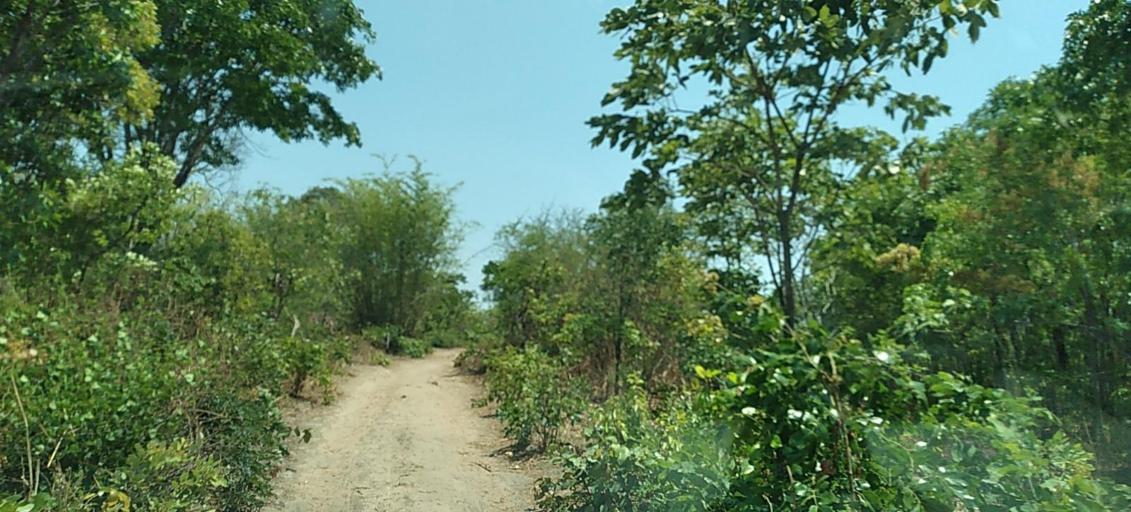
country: ZM
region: Copperbelt
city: Luanshya
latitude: -12.9893
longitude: 28.3283
